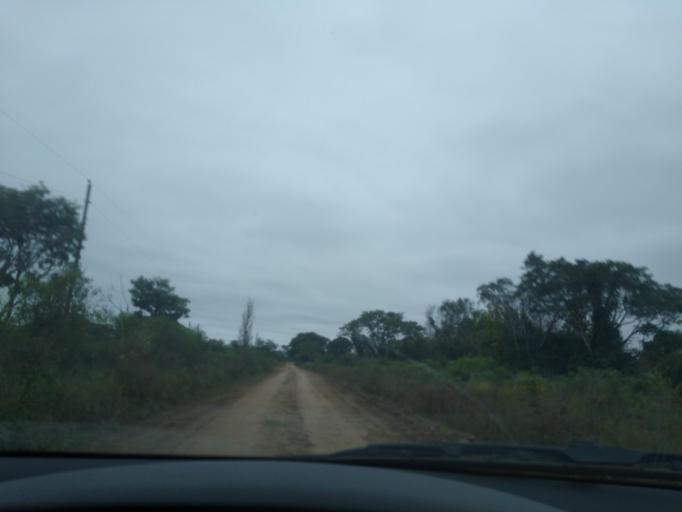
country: AR
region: Chaco
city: Colonia Benitez
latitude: -27.3732
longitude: -58.9452
